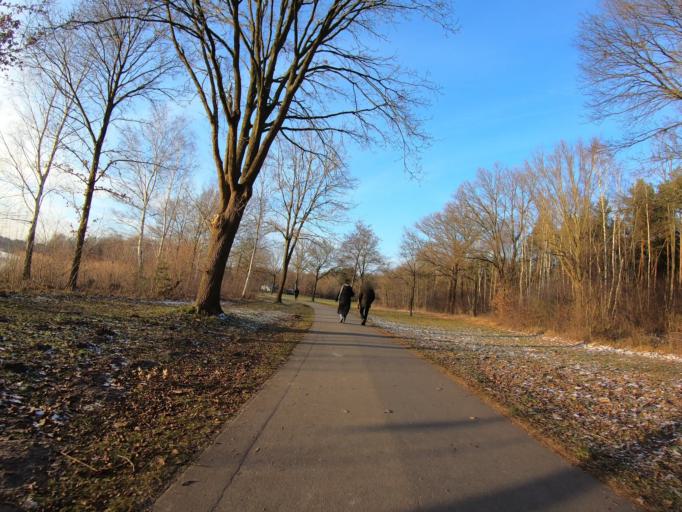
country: DE
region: Lower Saxony
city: Calberlah
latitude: 52.4539
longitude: 10.6292
